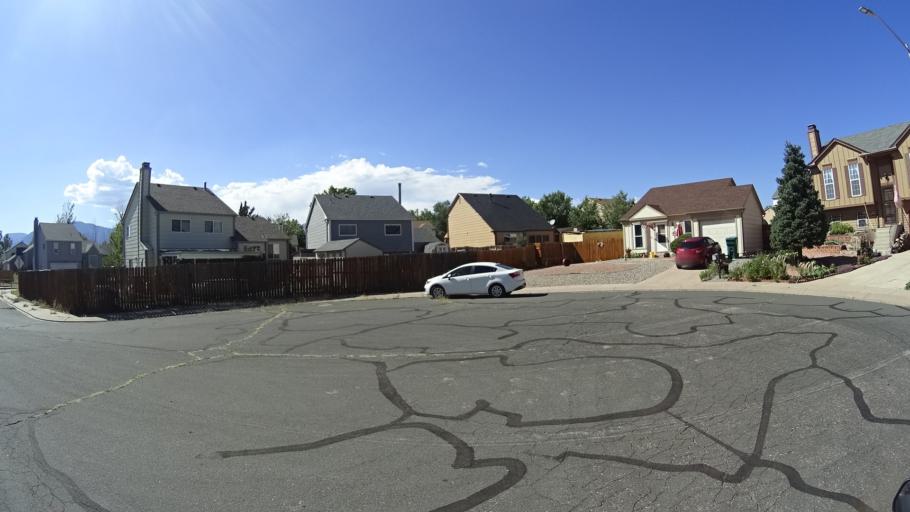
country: US
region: Colorado
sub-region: El Paso County
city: Stratmoor
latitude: 38.7941
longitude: -104.7368
